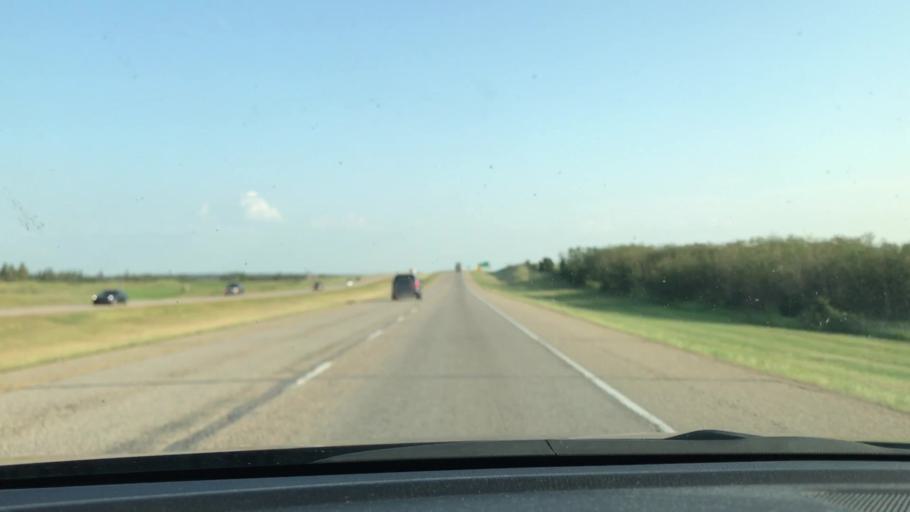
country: CA
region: Alberta
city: Ponoka
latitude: 52.5870
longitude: -113.6633
